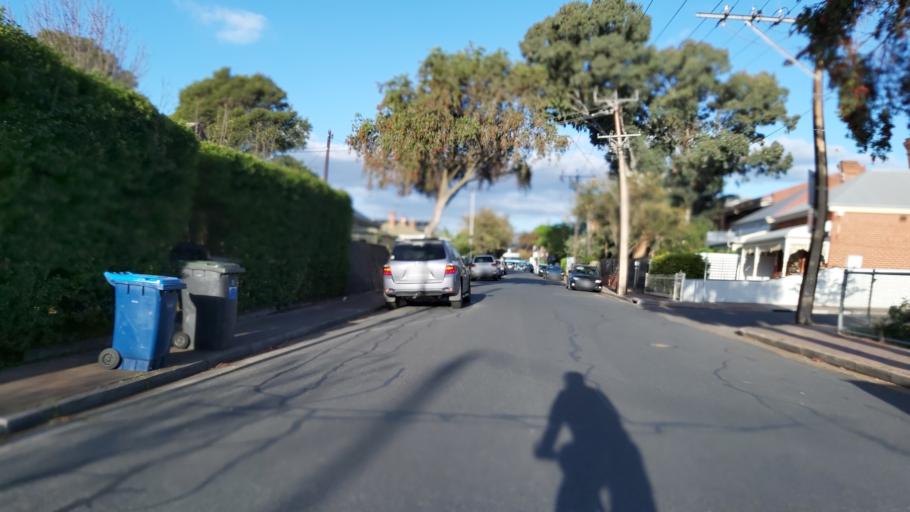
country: AU
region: South Australia
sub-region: Unley
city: Unley
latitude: -34.9484
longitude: 138.6050
